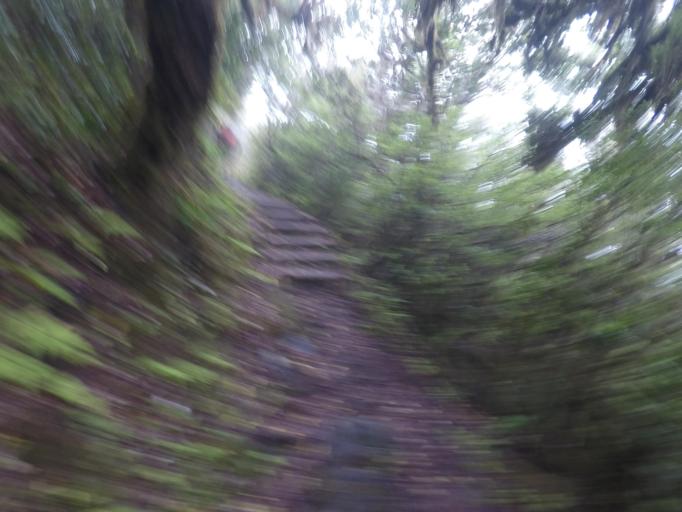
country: PT
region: Madeira
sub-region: Calheta
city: Arco da Calheta
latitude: 32.7744
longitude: -17.1227
